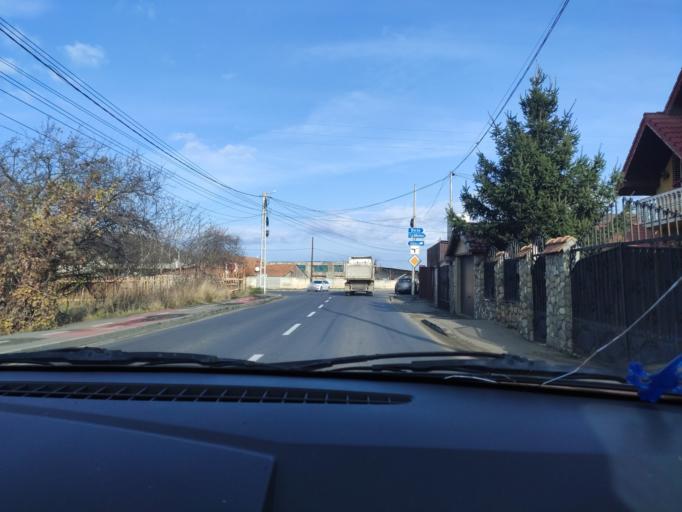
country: RO
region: Brasov
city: Codlea
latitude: 45.7038
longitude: 25.4566
